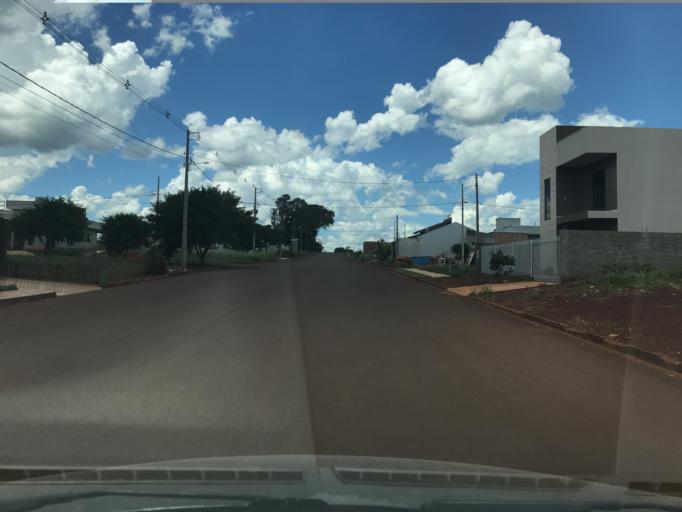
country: BR
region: Parana
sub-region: Palotina
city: Palotina
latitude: -24.2648
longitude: -53.8438
